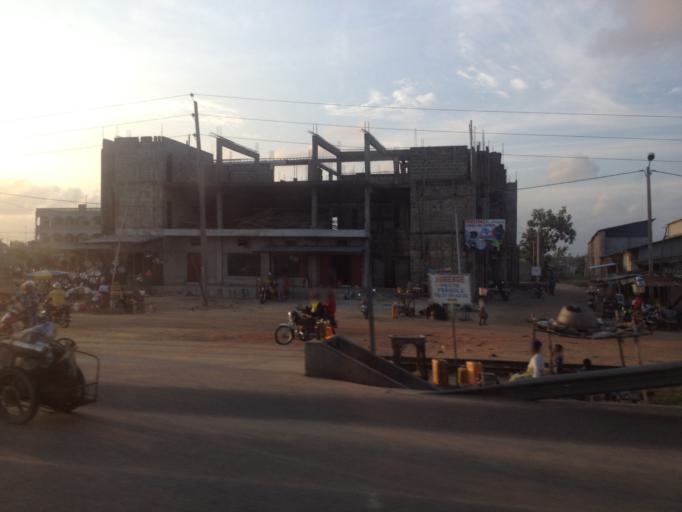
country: BJ
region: Littoral
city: Cotonou
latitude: 6.3725
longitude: 2.5404
